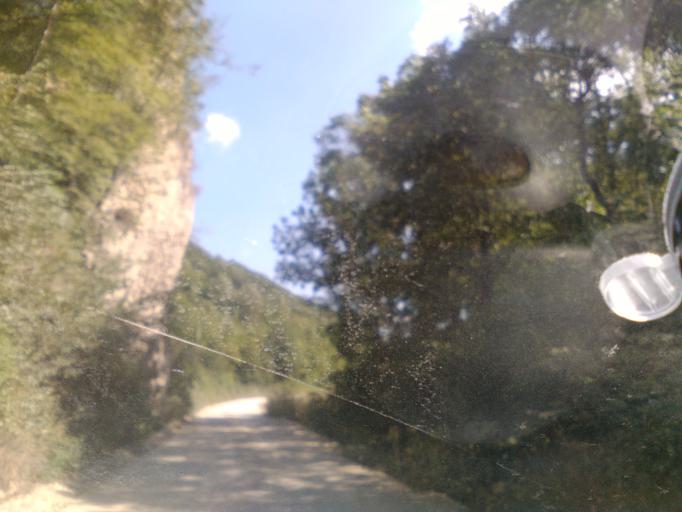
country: BA
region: Federation of Bosnia and Herzegovina
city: Orasac
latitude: 44.5080
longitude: 16.1278
